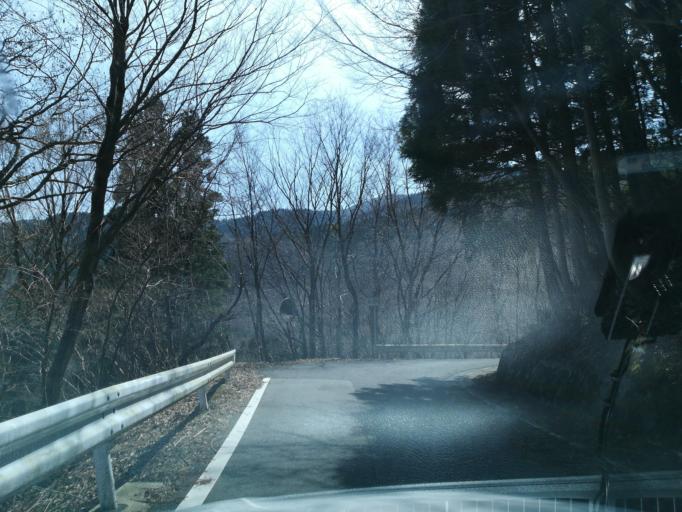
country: JP
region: Tokushima
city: Wakimachi
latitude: 33.8870
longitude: 134.0507
